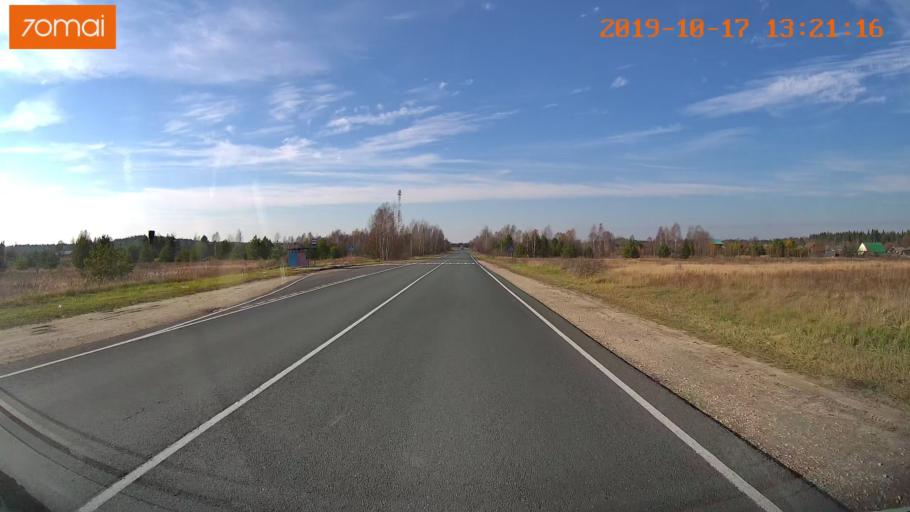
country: RU
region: Rjazan
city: Gus'-Zheleznyy
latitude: 55.0803
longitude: 41.0312
